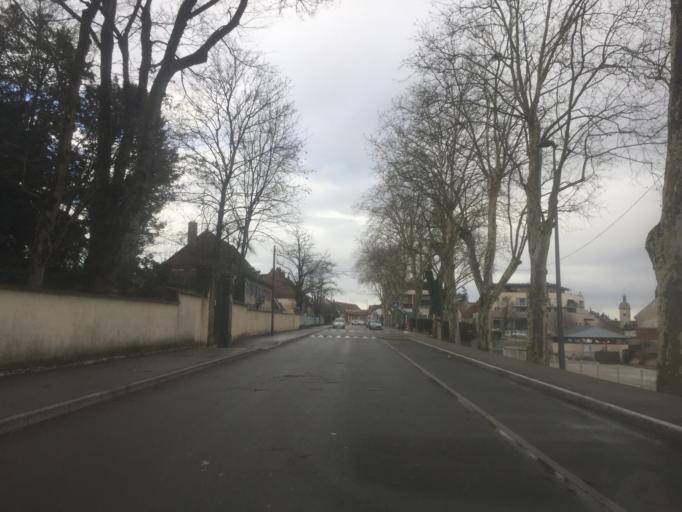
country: FR
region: Franche-Comte
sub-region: Departement du Doubs
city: Saint-Vit
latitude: 47.1805
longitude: 5.8048
